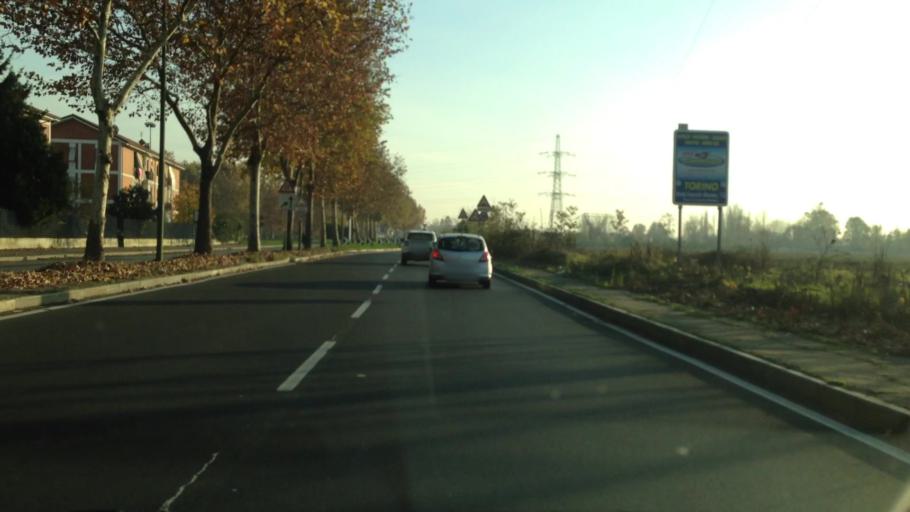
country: IT
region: Piedmont
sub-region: Provincia di Torino
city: Savonera
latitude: 45.1021
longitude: 7.6249
